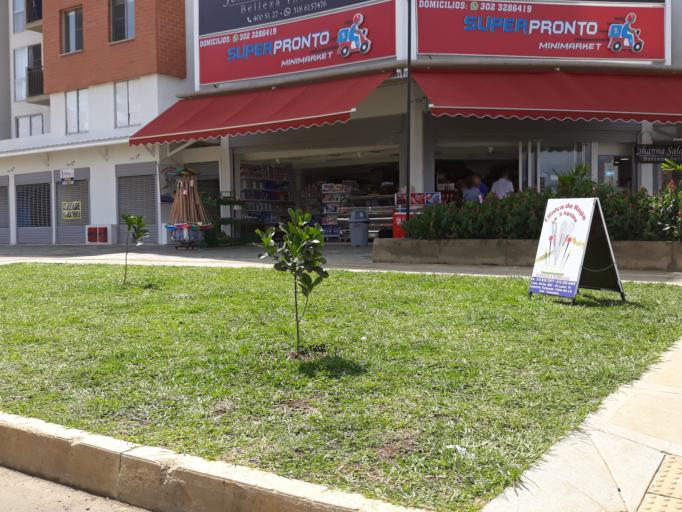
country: CO
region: Valle del Cauca
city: Cali
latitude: 3.3687
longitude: -76.5059
